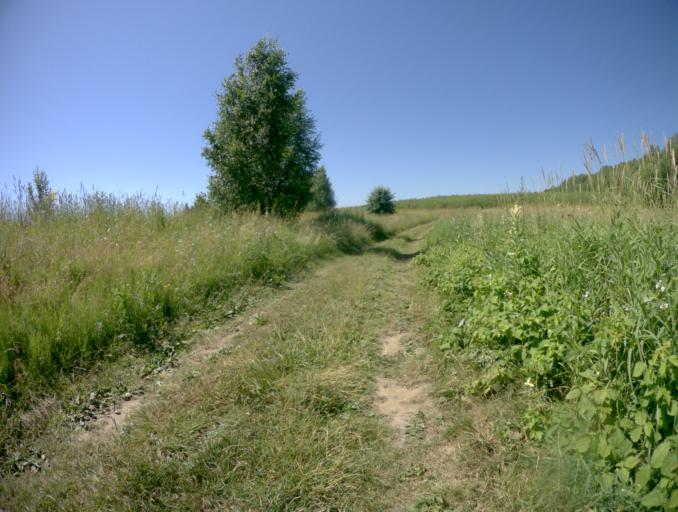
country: RU
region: Nizjnij Novgorod
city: Reshetikha
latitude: 56.1348
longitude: 43.2864
